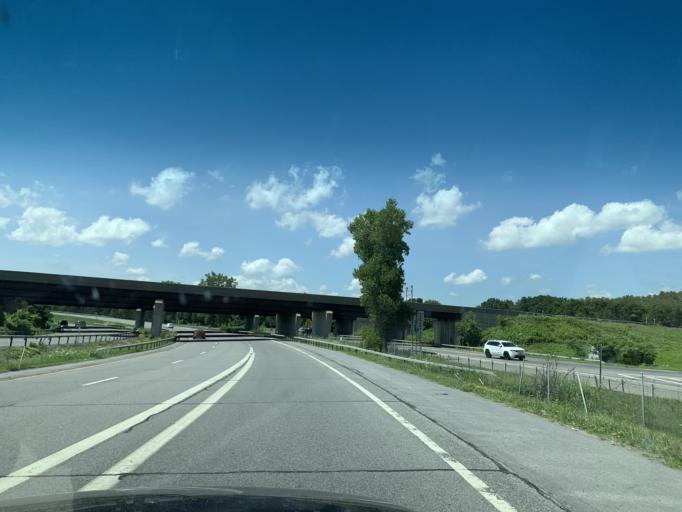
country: US
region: New York
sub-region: Oneida County
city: Utica
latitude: 43.1230
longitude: -75.2281
